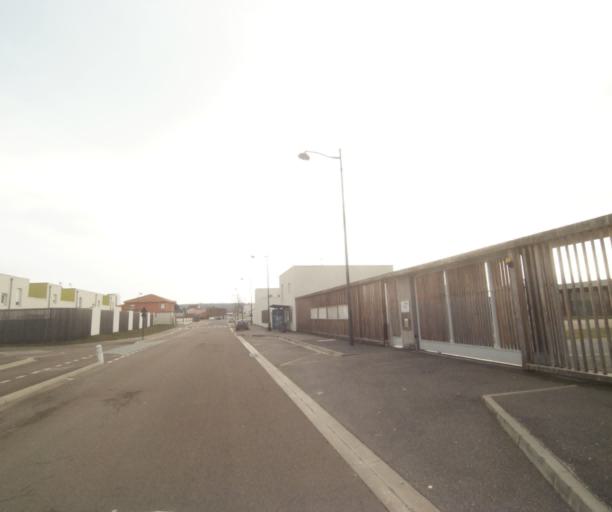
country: FR
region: Champagne-Ardenne
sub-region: Departement de la Haute-Marne
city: Bettancourt-la-Ferree
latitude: 48.6378
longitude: 4.9672
